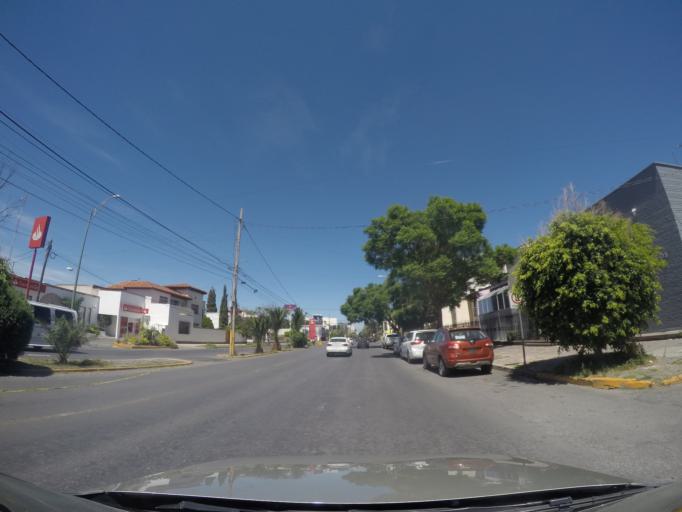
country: MX
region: San Luis Potosi
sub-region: San Luis Potosi
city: San Luis Potosi
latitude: 22.1493
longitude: -101.0027
